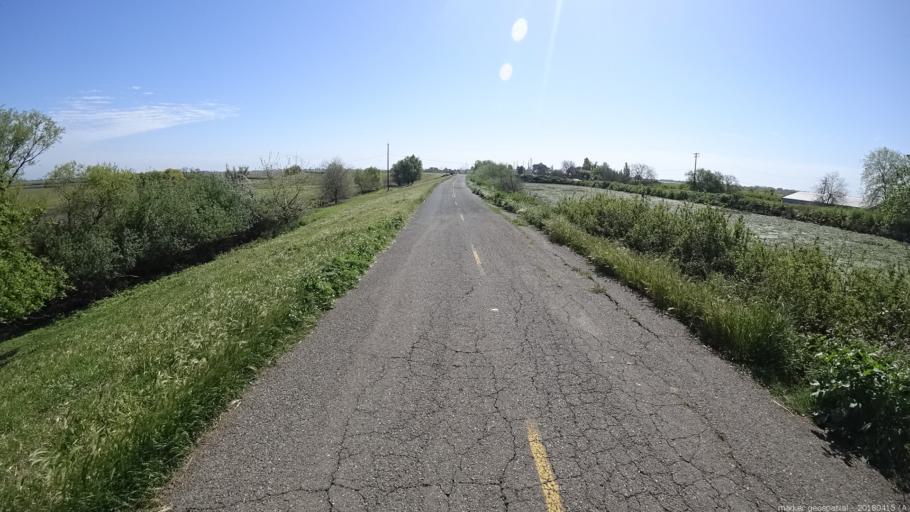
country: US
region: California
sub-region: Solano County
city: Rio Vista
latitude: 38.1174
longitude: -121.6319
